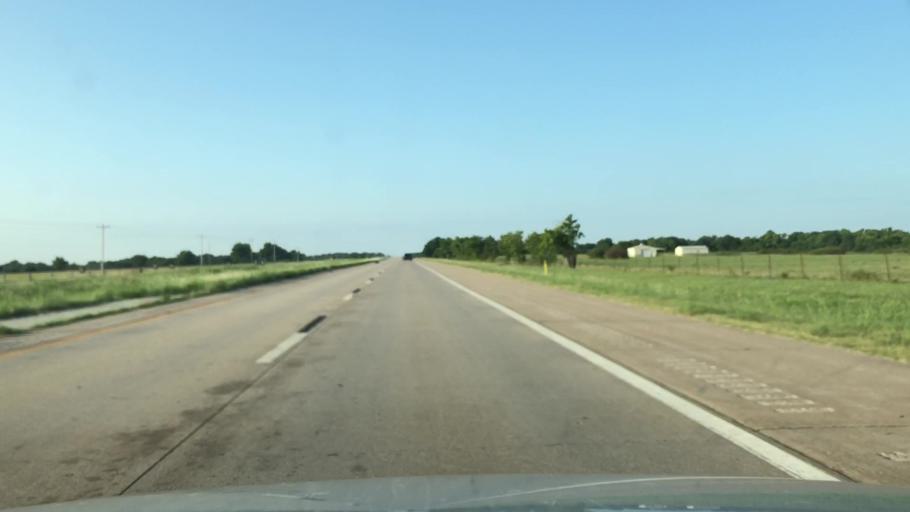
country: US
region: Oklahoma
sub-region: Osage County
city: Skiatook
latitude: 36.4489
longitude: -95.9207
